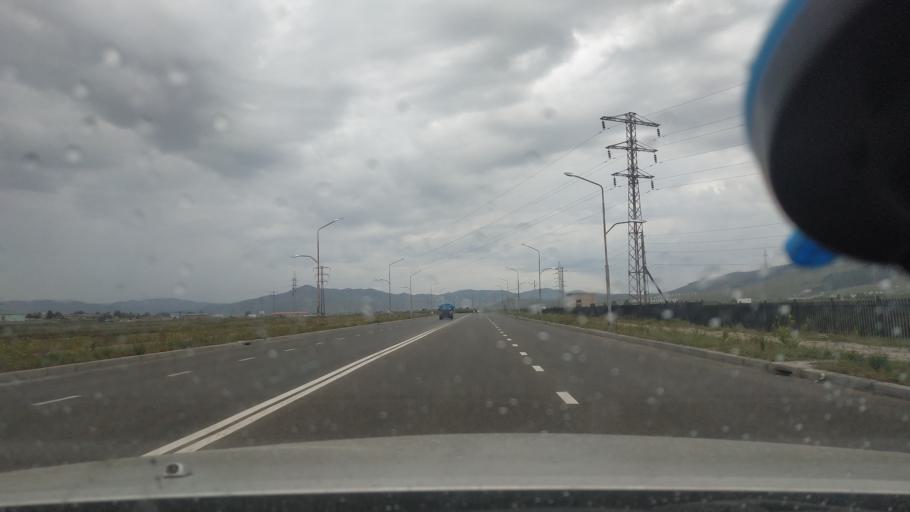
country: MN
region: Ulaanbaatar
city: Ulaanbaatar
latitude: 47.8996
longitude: 106.9956
